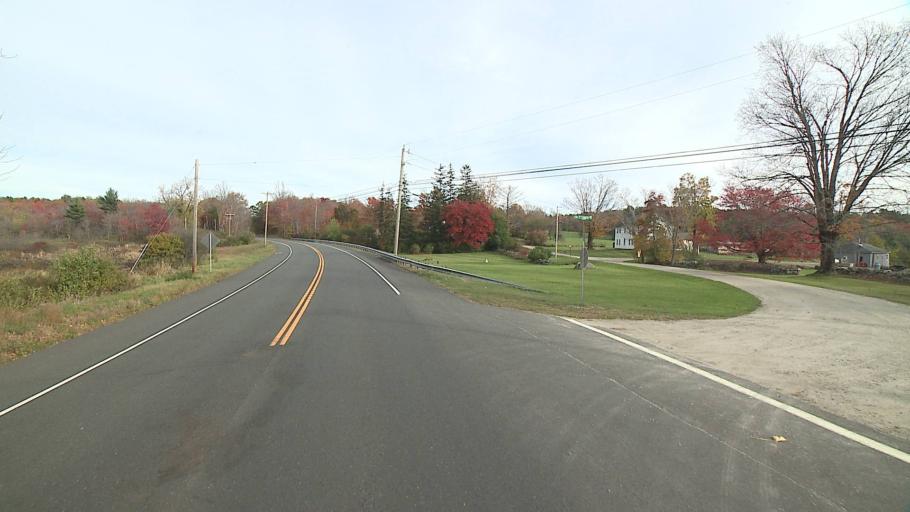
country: US
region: Connecticut
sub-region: Litchfield County
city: Winchester Center
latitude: 41.9796
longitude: -73.1594
